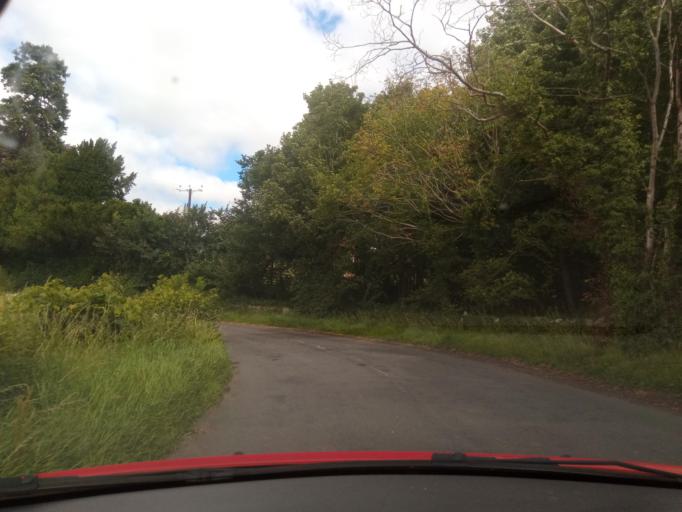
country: GB
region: Scotland
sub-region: The Scottish Borders
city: Kelso
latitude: 55.5297
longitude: -2.3570
